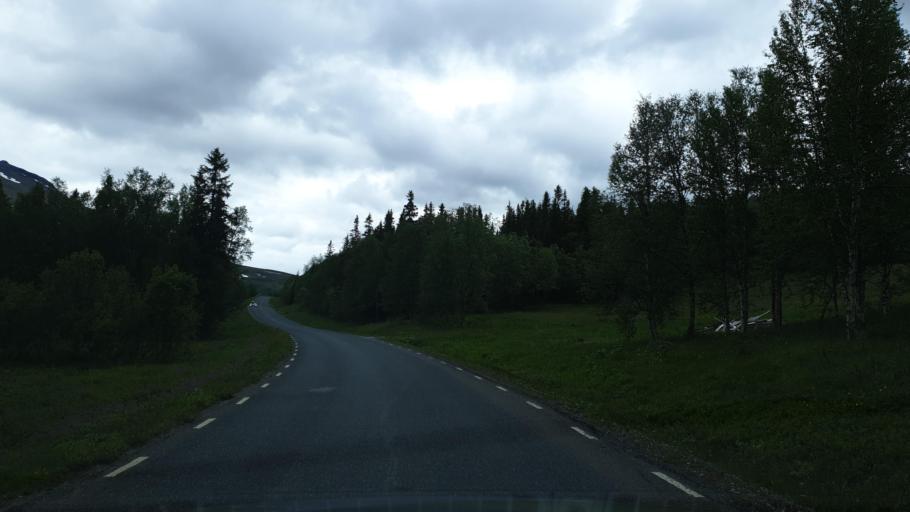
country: SE
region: Vaesterbotten
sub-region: Vilhelmina Kommun
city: Sjoberg
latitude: 65.2797
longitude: 15.3104
